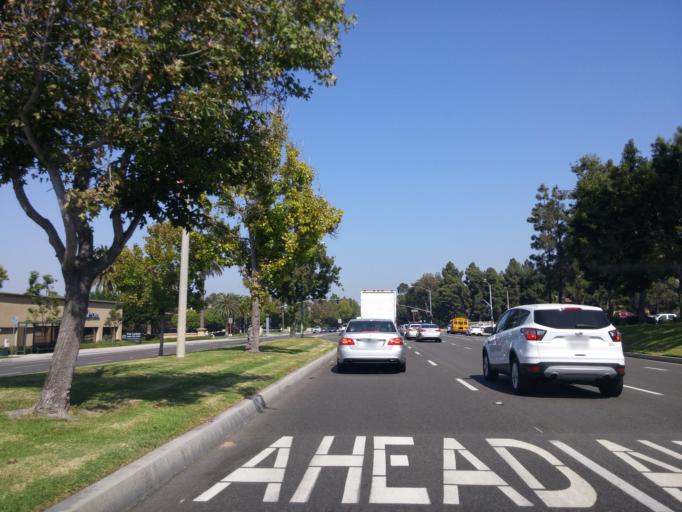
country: US
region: California
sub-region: Orange County
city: Irvine
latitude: 33.6831
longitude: -117.8092
